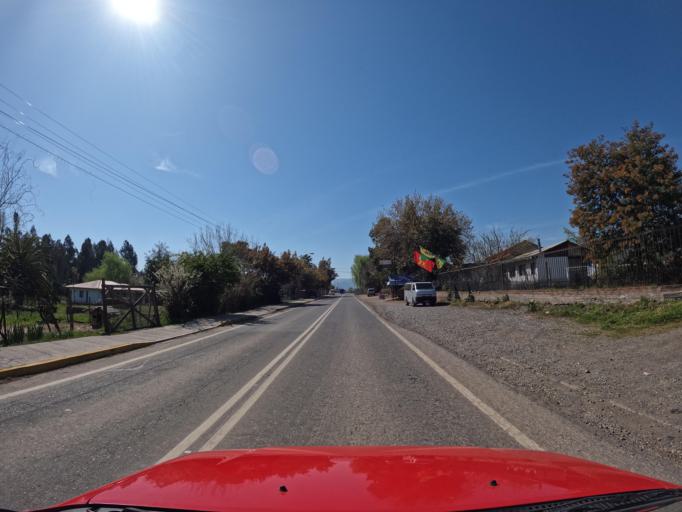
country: CL
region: Maule
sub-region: Provincia de Curico
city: Rauco
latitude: -35.0514
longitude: -71.4751
